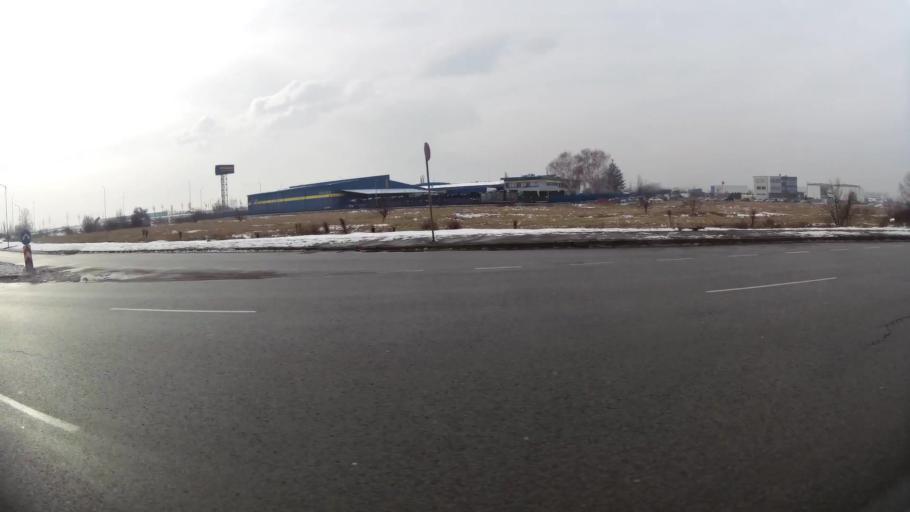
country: BG
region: Sofia-Capital
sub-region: Stolichna Obshtina
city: Sofia
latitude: 42.7073
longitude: 23.4012
